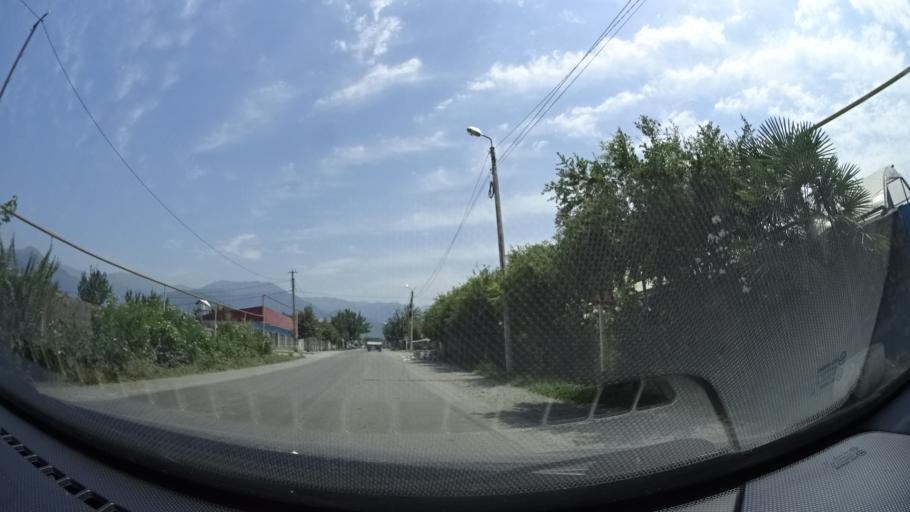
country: GE
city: Bagdadi
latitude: 41.8448
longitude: 46.1226
